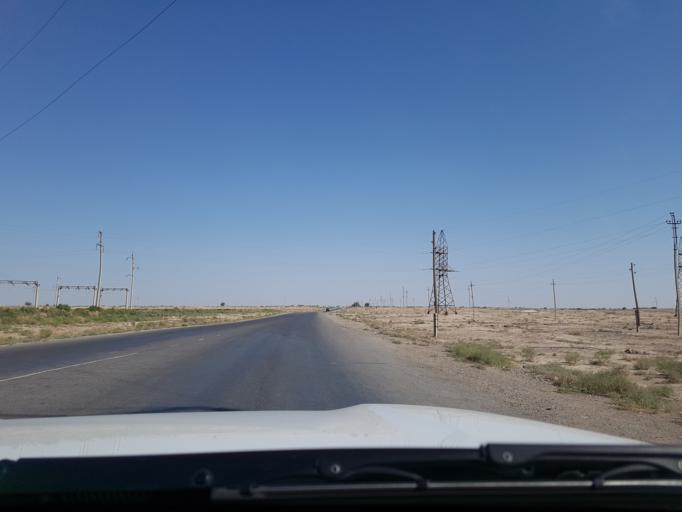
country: IR
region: Razavi Khorasan
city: Sarakhs
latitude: 36.5239
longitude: 61.2369
